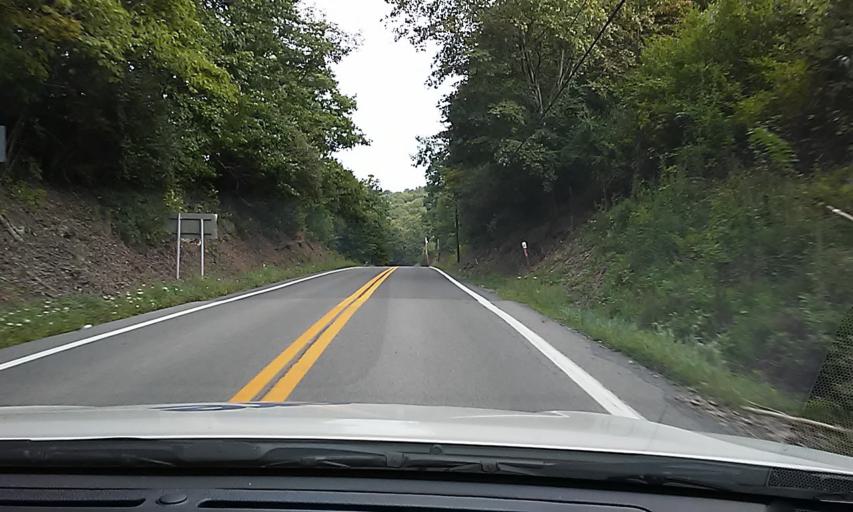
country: US
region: West Virginia
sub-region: Marion County
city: Mannington
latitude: 39.6586
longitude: -80.4000
